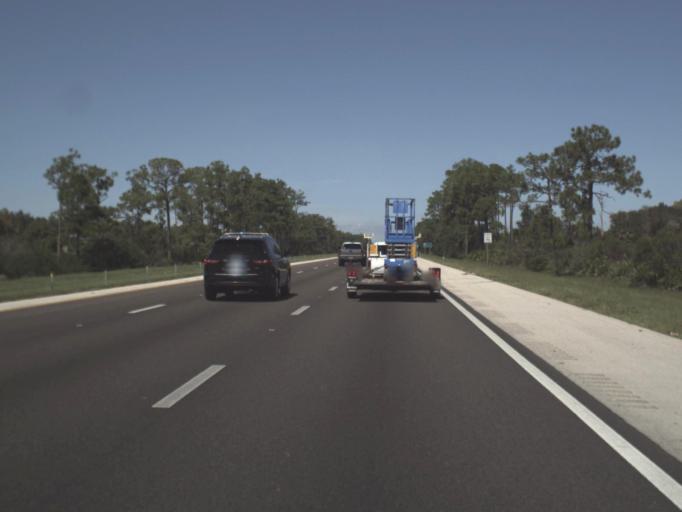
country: US
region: Florida
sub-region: Lee County
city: Gateway
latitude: 26.5570
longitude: -81.7945
